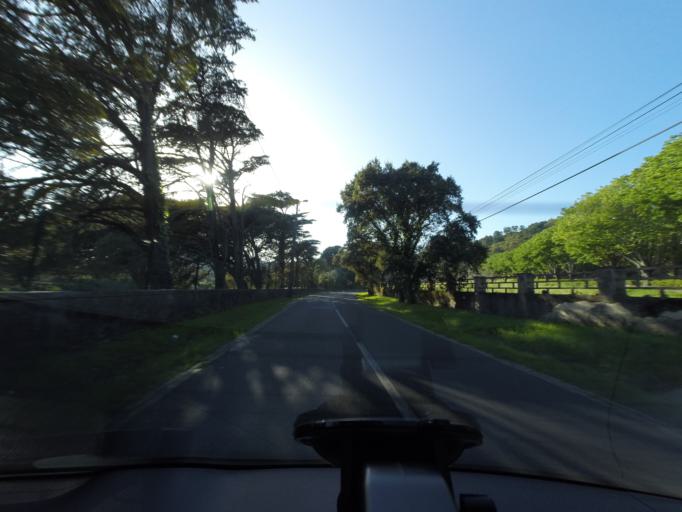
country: PT
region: Lisbon
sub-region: Sintra
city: Sintra
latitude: 38.7669
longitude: -9.3905
